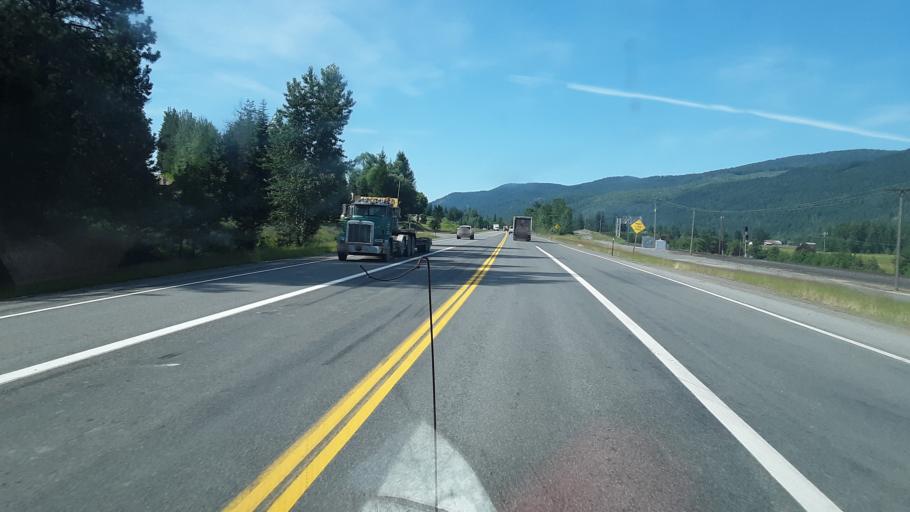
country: US
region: Idaho
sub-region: Bonner County
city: Ponderay
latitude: 48.4084
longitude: -116.5256
